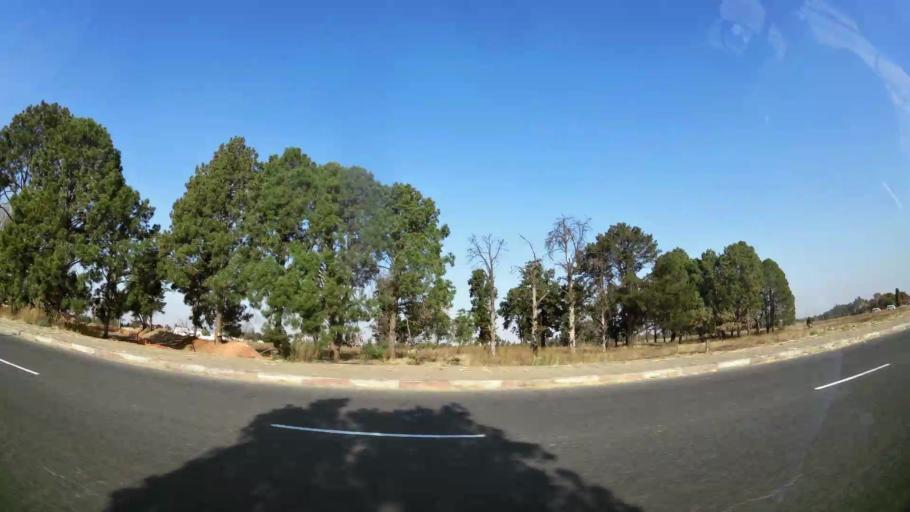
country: ZA
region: Gauteng
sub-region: West Rand District Municipality
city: Randfontein
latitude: -26.1737
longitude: 27.7105
